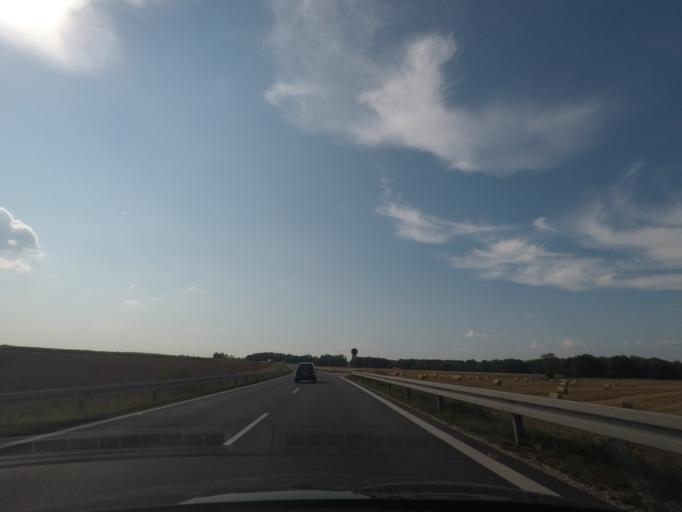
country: PL
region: Silesian Voivodeship
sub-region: Powiat pszczynski
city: Piasek
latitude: 50.0003
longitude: 18.9358
